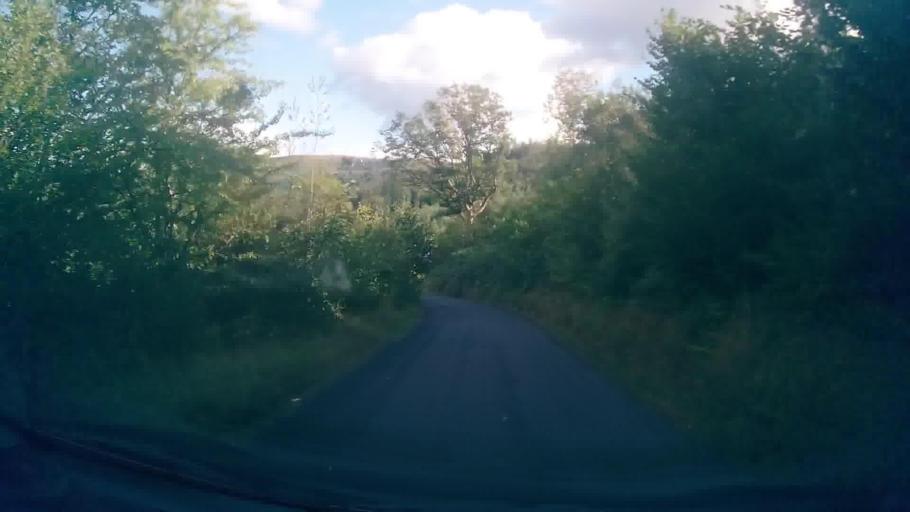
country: GB
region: Wales
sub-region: Merthyr Tydfil County Borough
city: Merthyr Tydfil
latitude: 51.8443
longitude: -3.3677
